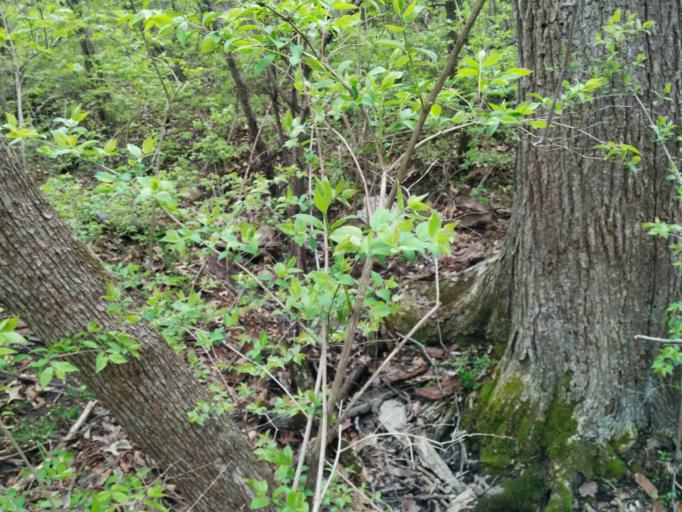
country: US
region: Illinois
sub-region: DuPage County
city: Burr Ridge
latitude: 41.7132
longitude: -87.9029
